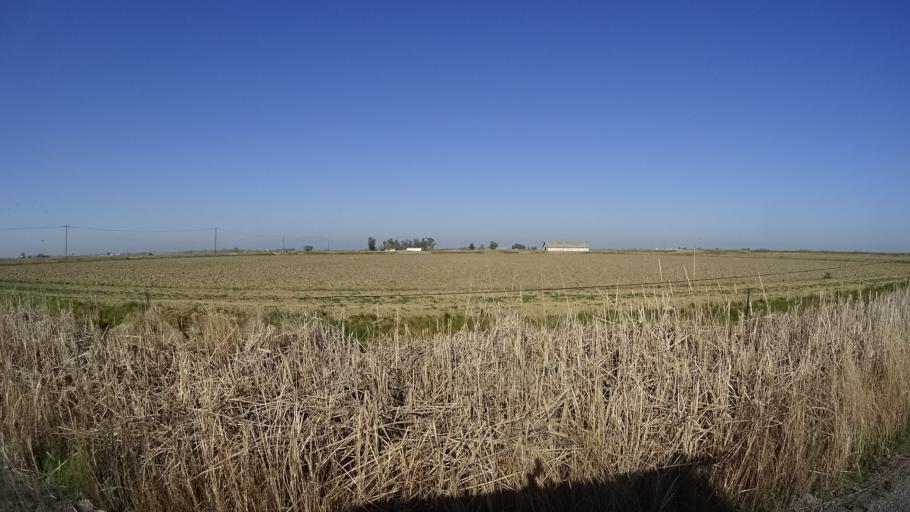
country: US
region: California
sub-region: Glenn County
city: Willows
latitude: 39.5542
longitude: -122.1321
